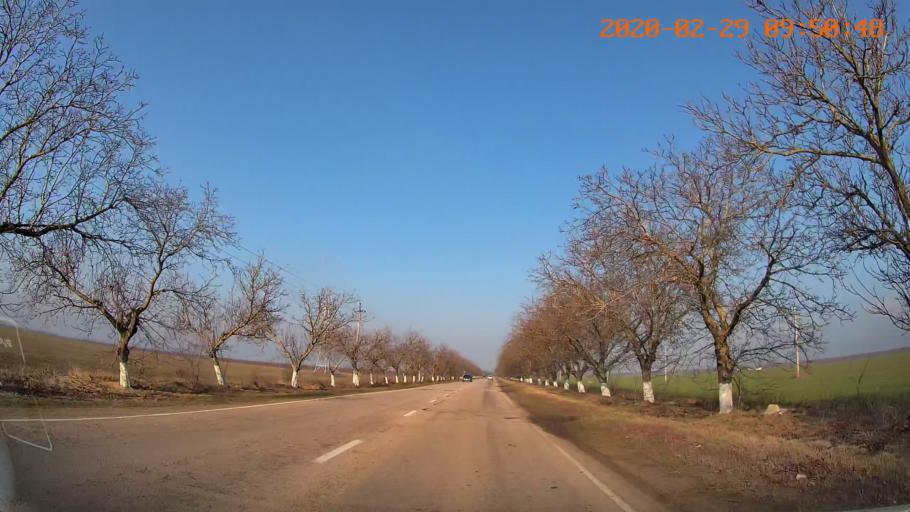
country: MD
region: Telenesti
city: Slobozia
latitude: 46.7035
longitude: 29.7494
